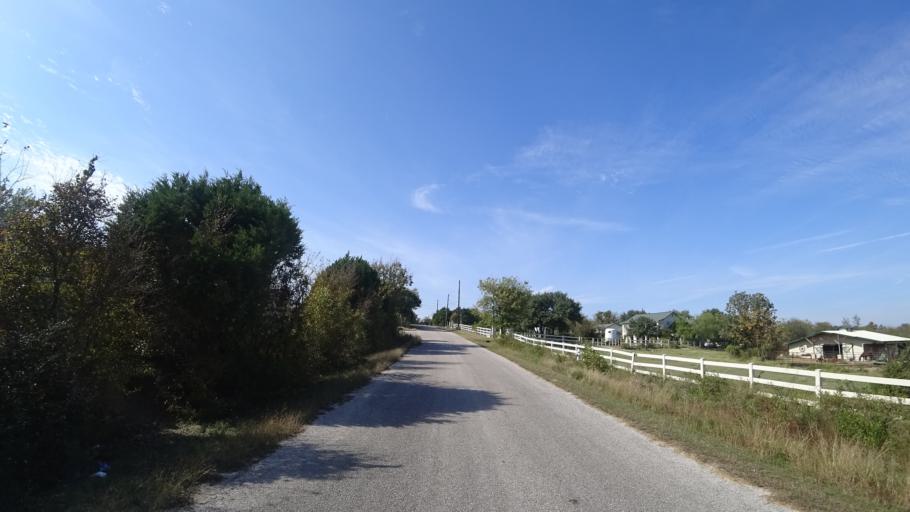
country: US
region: Texas
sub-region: Travis County
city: Pflugerville
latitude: 30.3975
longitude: -97.6352
